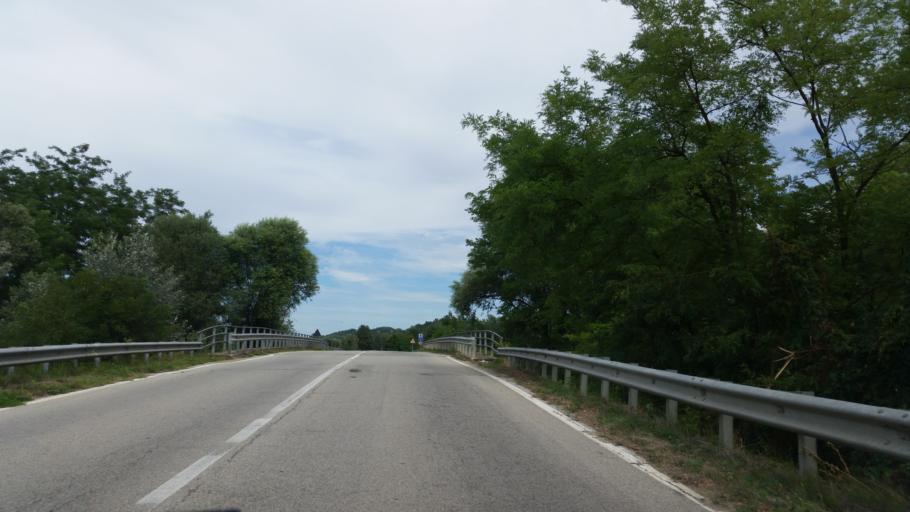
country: IT
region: Piedmont
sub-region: Provincia di Asti
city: Celle Enomondo
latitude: 44.8725
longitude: 8.1178
